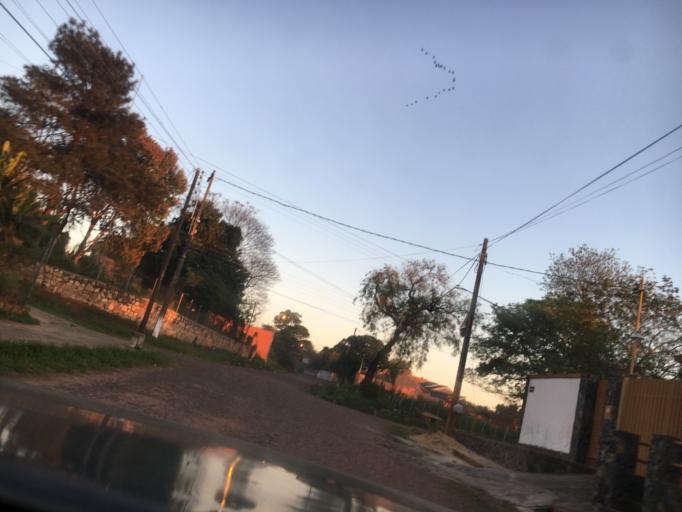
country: PY
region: Central
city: Villa Elisa
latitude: -25.3581
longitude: -57.5924
